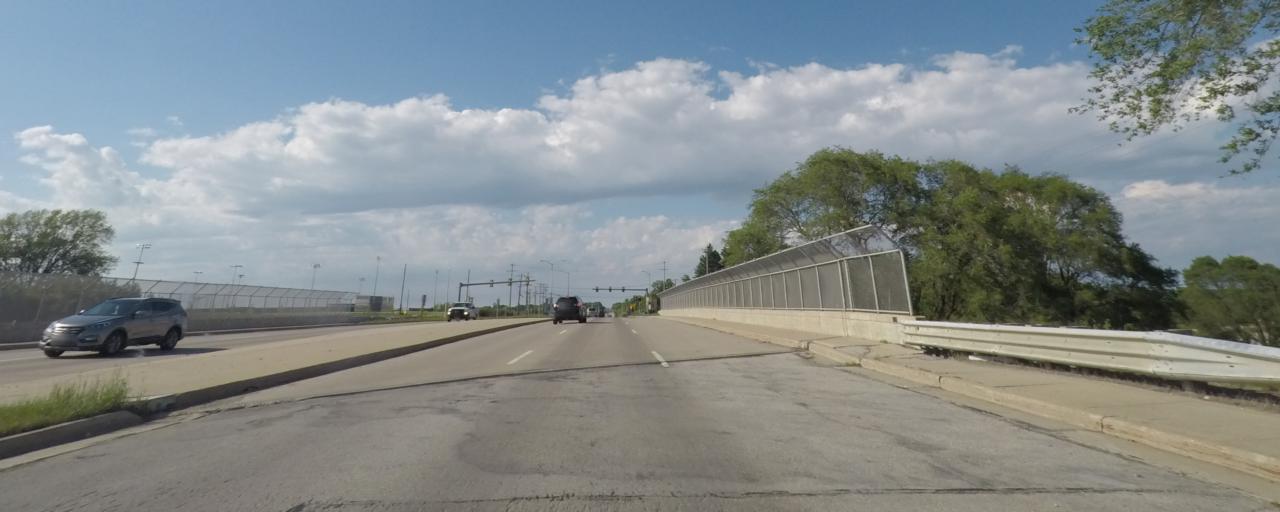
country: US
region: Wisconsin
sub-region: Milwaukee County
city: Greendale
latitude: 42.9184
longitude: -88.0090
